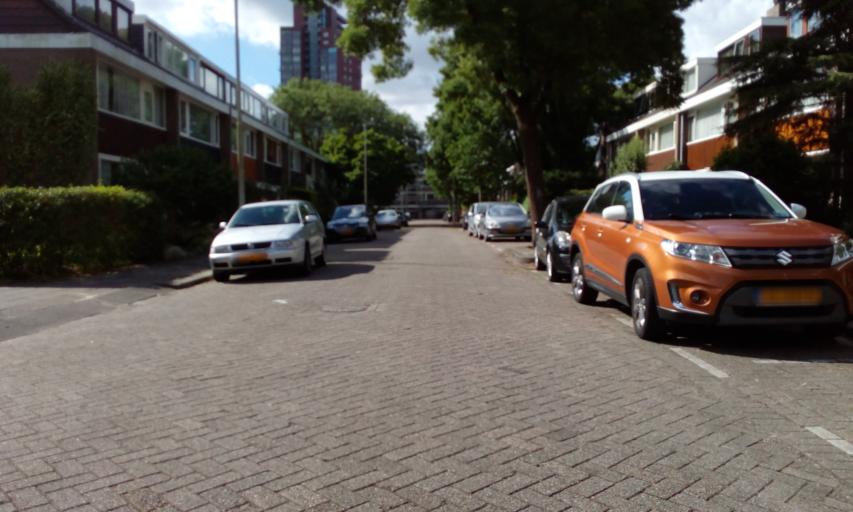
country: NL
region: South Holland
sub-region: Gemeente Rotterdam
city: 's-Gravenland
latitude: 51.9402
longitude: 4.5418
